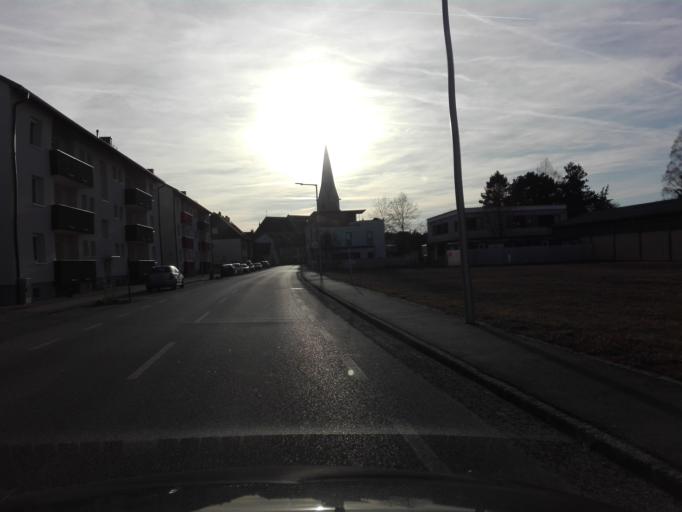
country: AT
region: Lower Austria
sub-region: Politischer Bezirk Amstetten
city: Sankt Valentin
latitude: 48.1763
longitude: 14.5359
